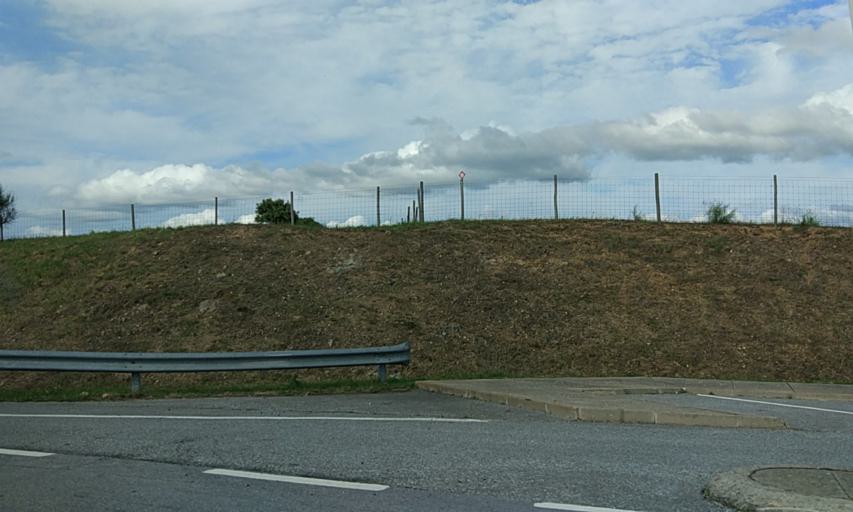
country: PT
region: Evora
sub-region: Evora
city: Evora
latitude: 38.6441
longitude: -7.8555
